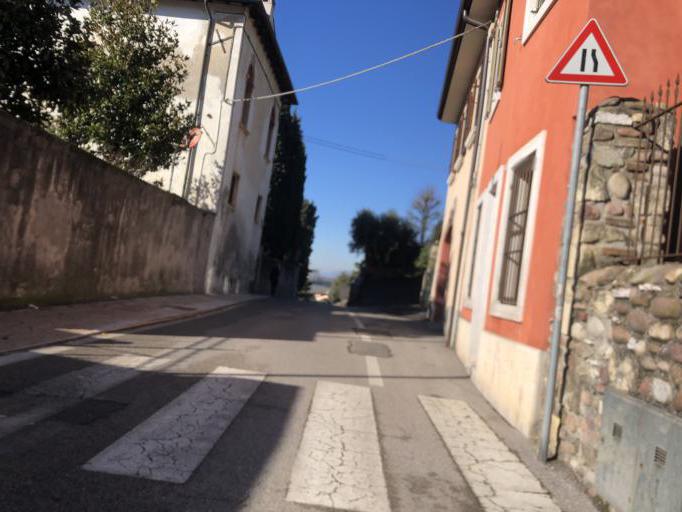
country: IT
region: Veneto
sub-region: Provincia di Verona
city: Sona
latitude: 45.4349
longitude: 10.8314
